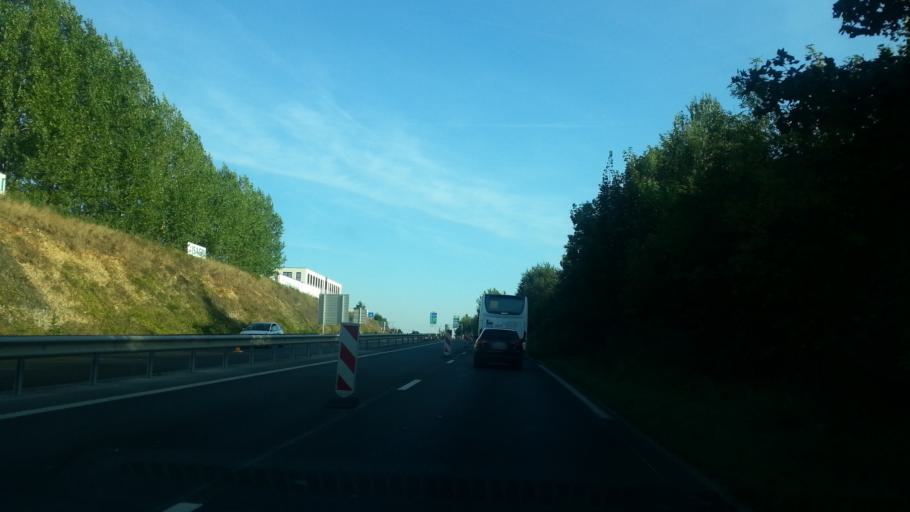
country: FR
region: Picardie
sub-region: Departement de l'Oise
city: Tille
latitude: 49.4560
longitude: 2.0932
